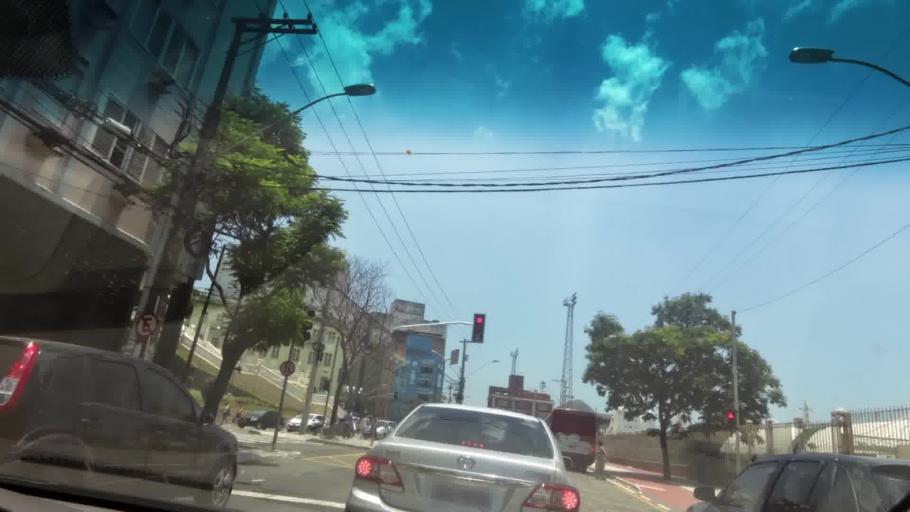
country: BR
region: Espirito Santo
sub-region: Vitoria
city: Vitoria
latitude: -20.3221
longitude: -40.3401
